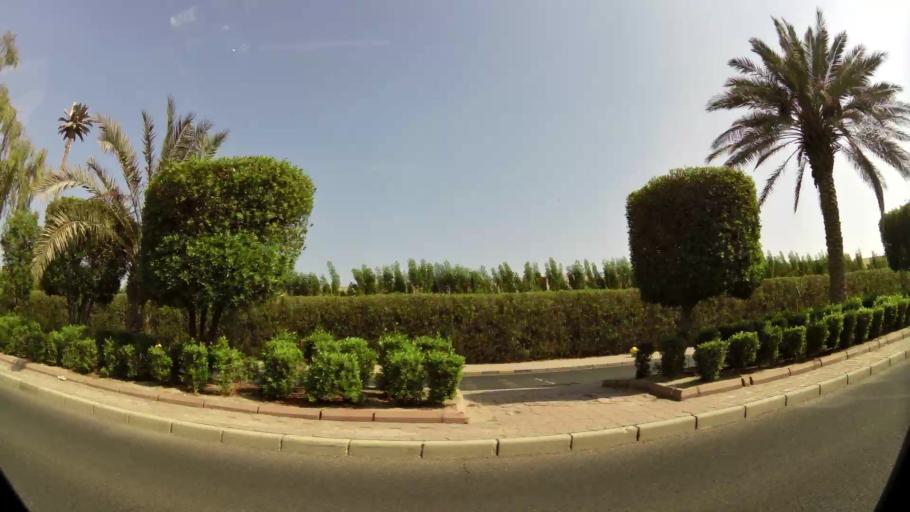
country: KW
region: Al Ahmadi
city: Al Manqaf
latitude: 29.1080
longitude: 48.1369
